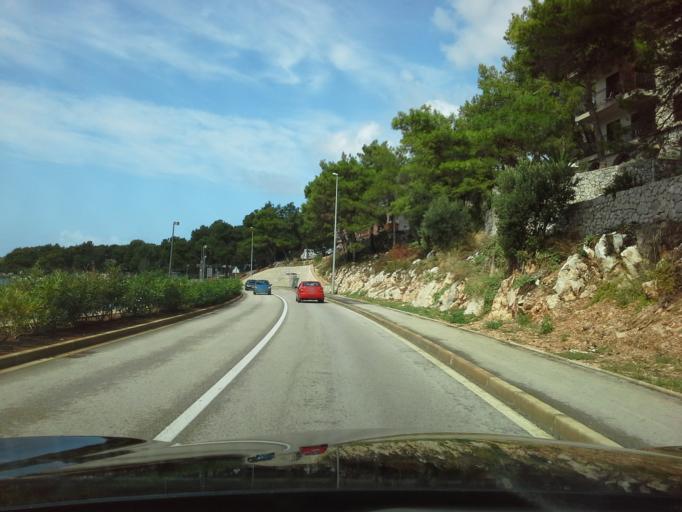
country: HR
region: Primorsko-Goranska
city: Mali Losinj
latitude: 44.5528
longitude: 14.4479
